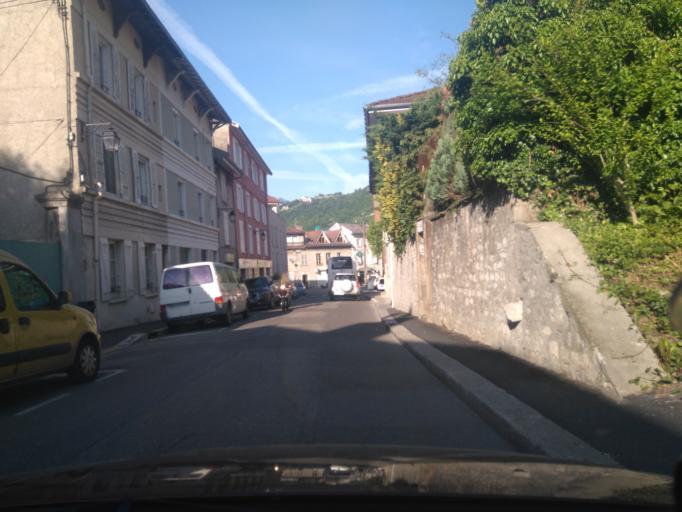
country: FR
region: Rhone-Alpes
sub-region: Departement de l'Isere
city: La Tronche
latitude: 45.2074
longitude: 5.7466
